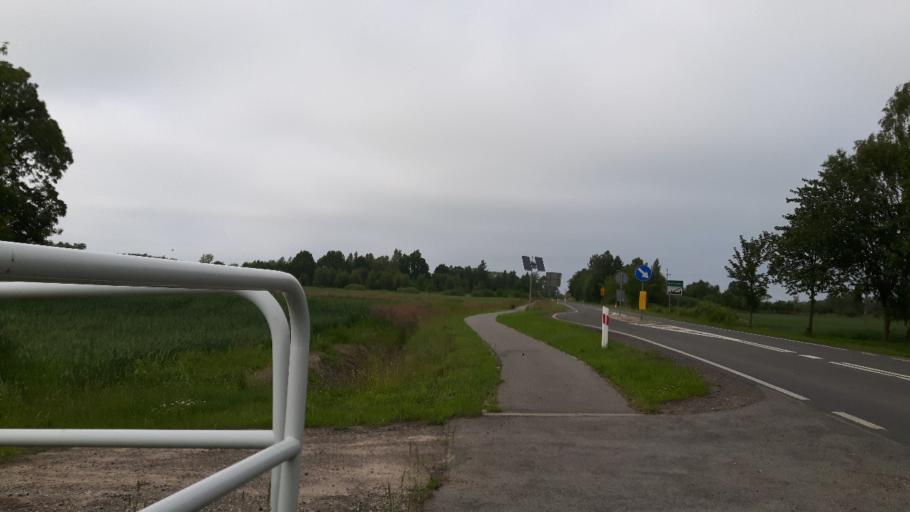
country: PL
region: West Pomeranian Voivodeship
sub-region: Powiat koszalinski
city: Sianow
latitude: 54.3253
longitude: 16.3102
